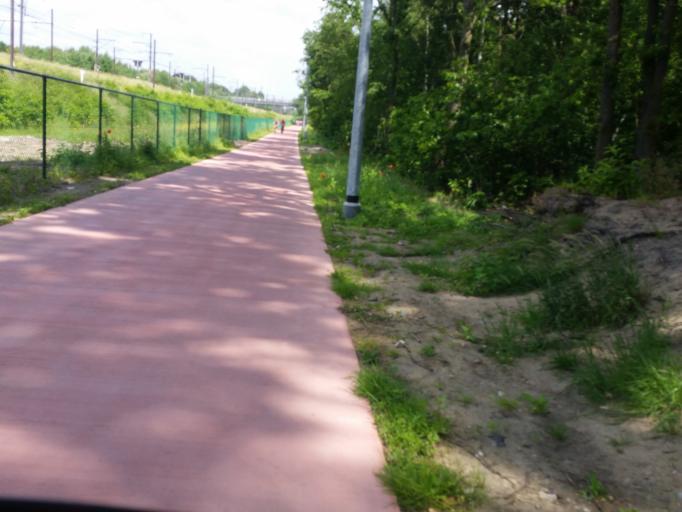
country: BE
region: Flanders
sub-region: Provincie Antwerpen
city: Mechelen
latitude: 51.0489
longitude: 4.4940
